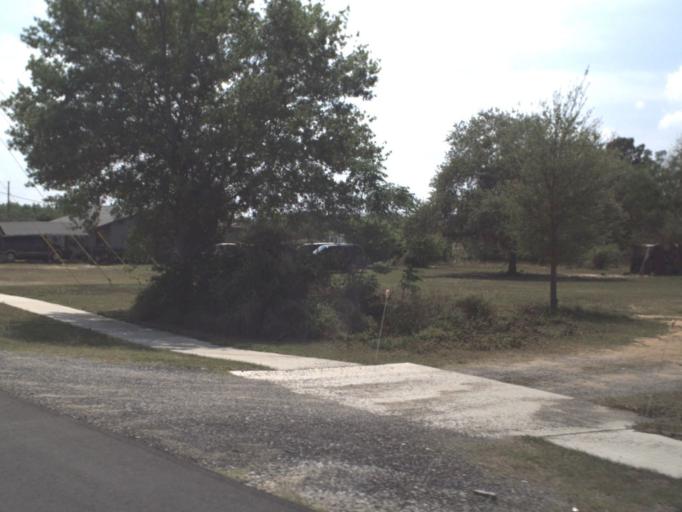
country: US
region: Florida
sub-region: Lake County
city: Tavares
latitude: 28.7813
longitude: -81.7490
